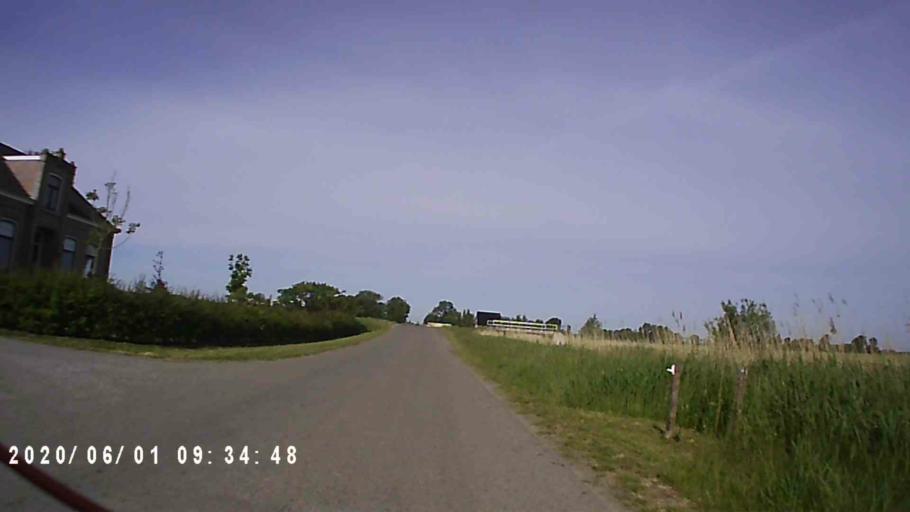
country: NL
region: Friesland
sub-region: Gemeente Leeuwarderadeel
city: Stiens
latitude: 53.2611
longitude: 5.7096
